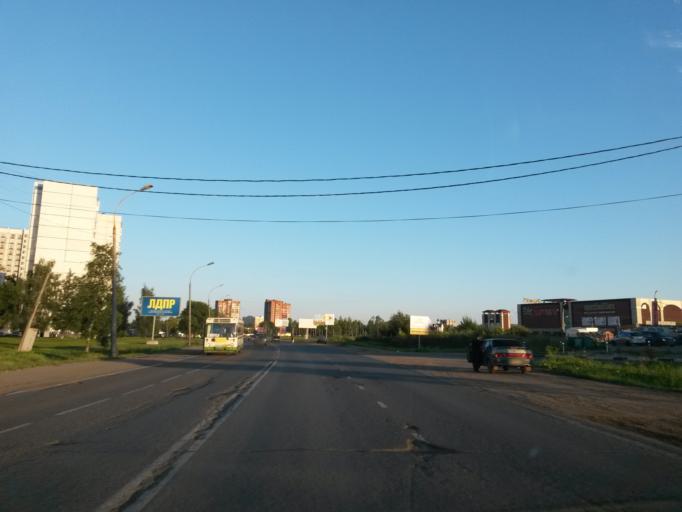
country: RU
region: Jaroslavl
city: Yaroslavl
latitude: 57.7012
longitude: 39.7602
